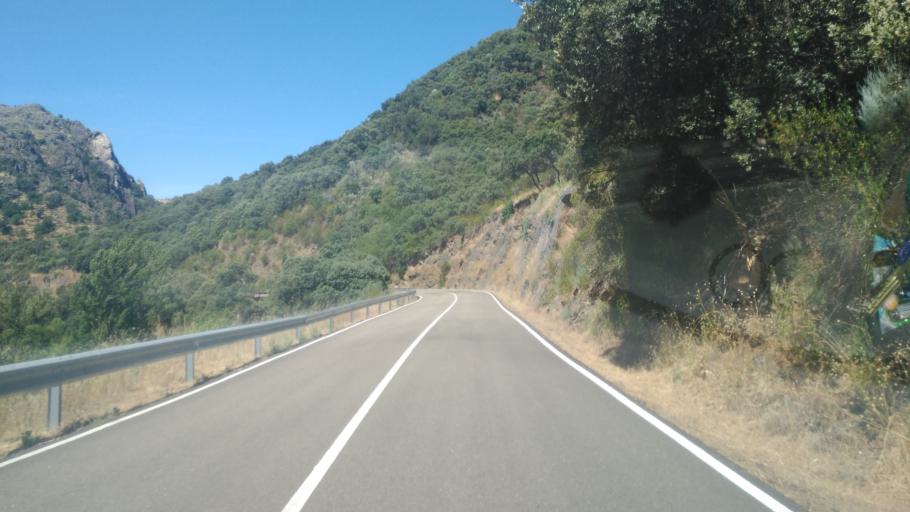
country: ES
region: Castille and Leon
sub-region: Provincia de Salamanca
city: Mieza
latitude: 41.1856
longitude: -6.6688
